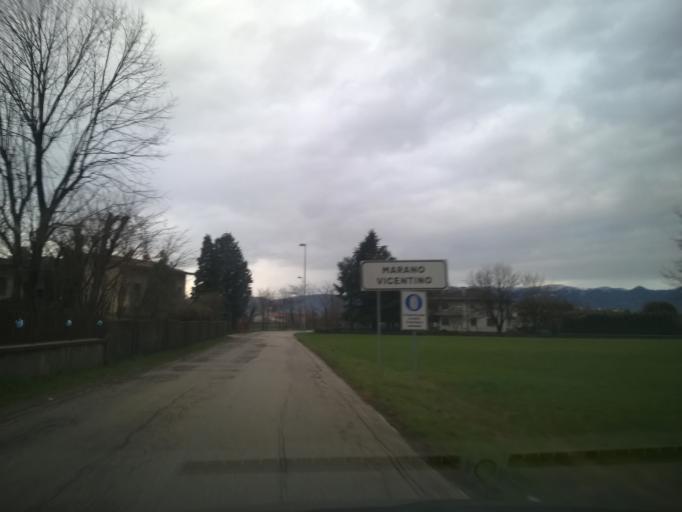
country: IT
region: Veneto
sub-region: Provincia di Vicenza
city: Marano Vicentino
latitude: 45.7008
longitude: 11.4429
